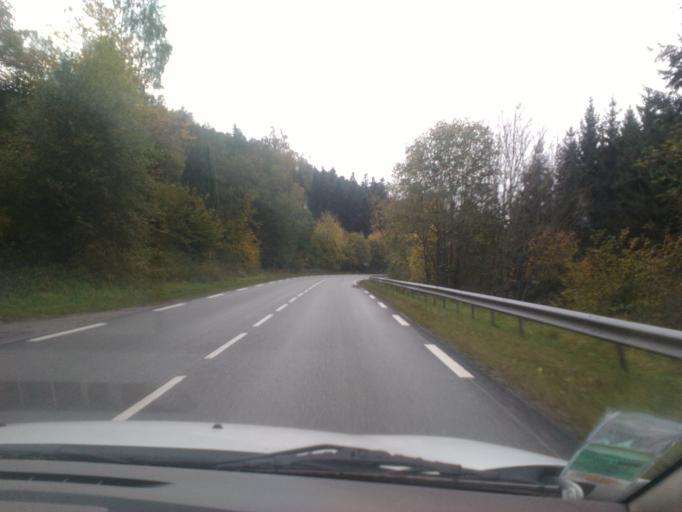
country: FR
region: Lorraine
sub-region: Departement des Vosges
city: Corcieux
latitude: 48.1394
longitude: 6.9164
